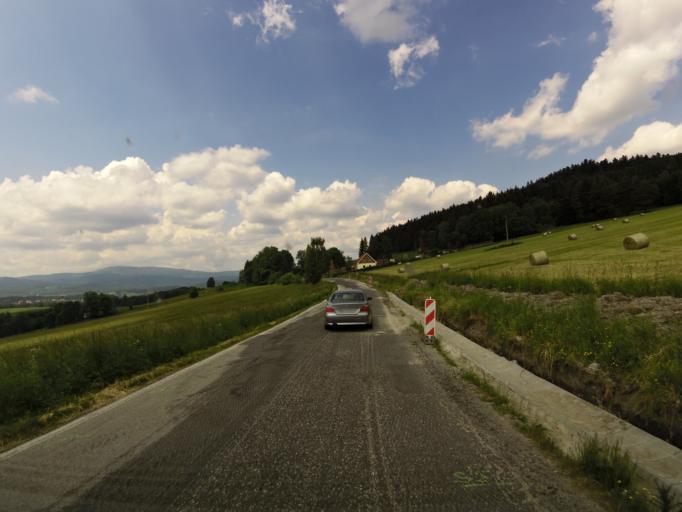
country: CZ
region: Jihocesky
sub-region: Okres Cesky Krumlov
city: Horni Plana
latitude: 48.7962
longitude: 13.9883
